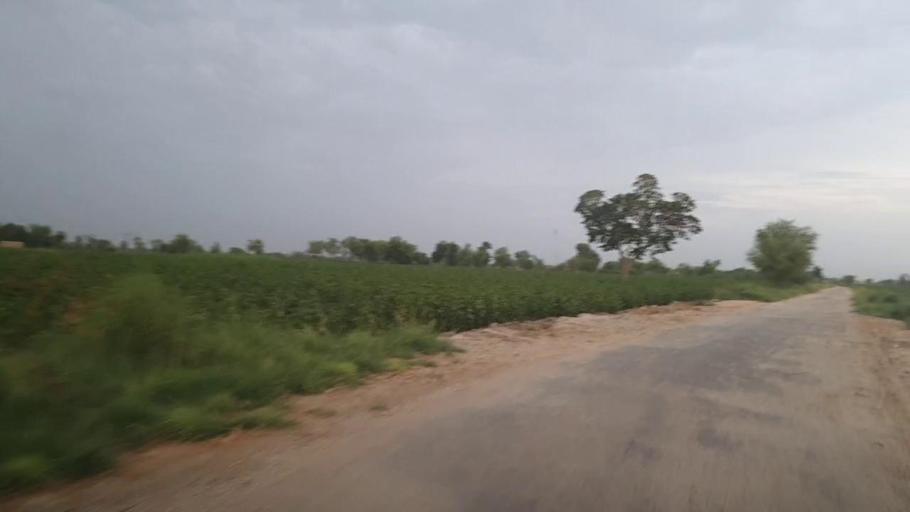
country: PK
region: Sindh
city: Karaundi
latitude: 27.0078
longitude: 68.3441
